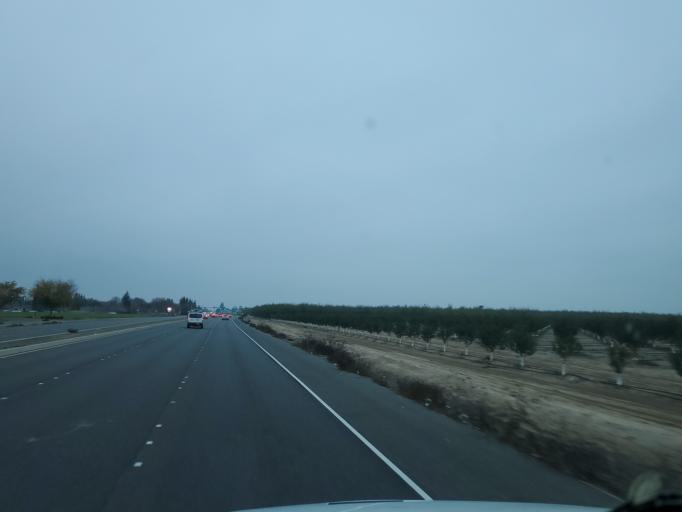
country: US
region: California
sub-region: Stanislaus County
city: Del Rio
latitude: 37.7007
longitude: -121.0071
